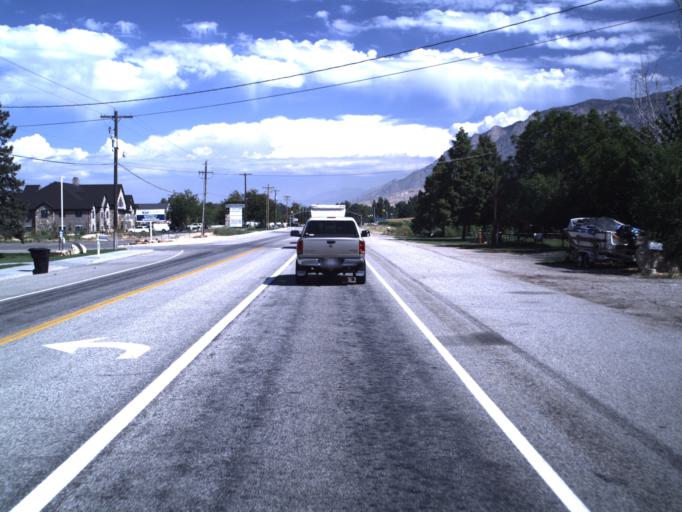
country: US
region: Utah
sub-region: Weber County
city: Farr West
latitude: 41.2862
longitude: -112.0279
